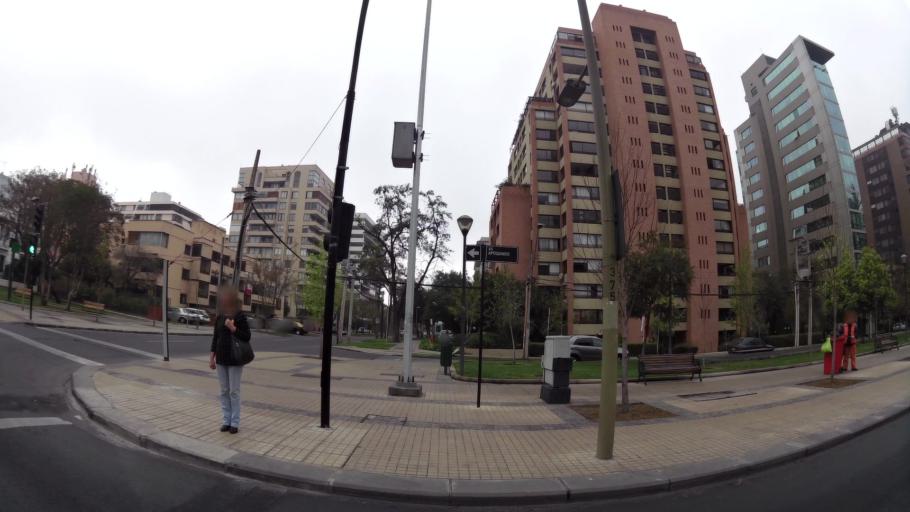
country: CL
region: Santiago Metropolitan
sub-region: Provincia de Santiago
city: Villa Presidente Frei, Nunoa, Santiago, Chile
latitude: -33.4109
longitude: -70.5743
